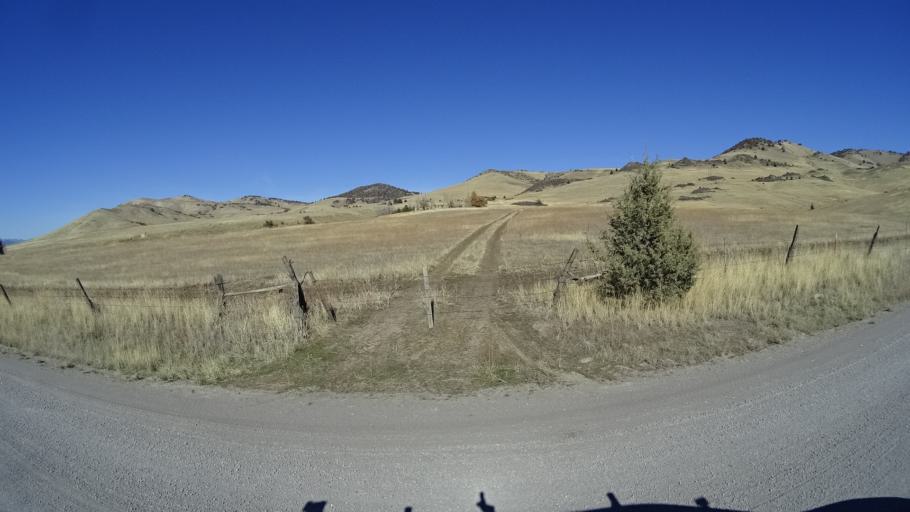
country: US
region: California
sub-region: Siskiyou County
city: Montague
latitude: 41.8299
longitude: -122.3658
